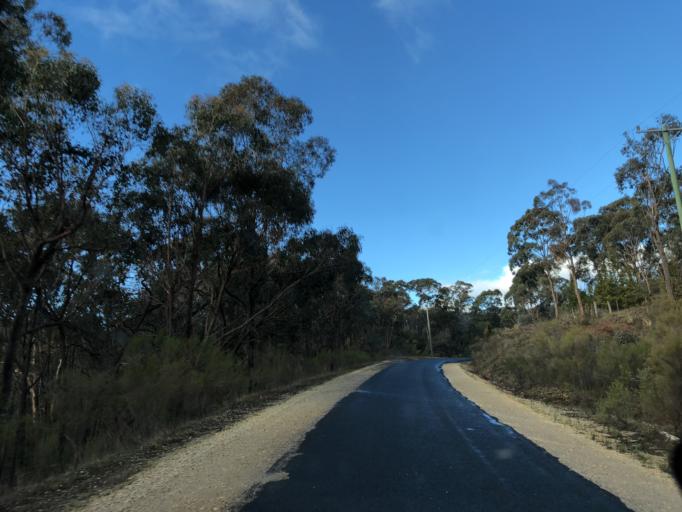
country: AU
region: Victoria
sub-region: Mount Alexander
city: Castlemaine
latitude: -37.2075
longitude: 144.2814
